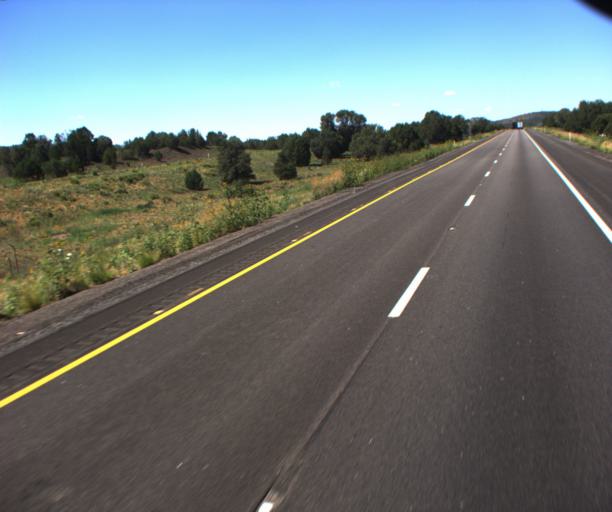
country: US
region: Arizona
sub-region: Mohave County
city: Peach Springs
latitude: 35.2127
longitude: -113.2613
